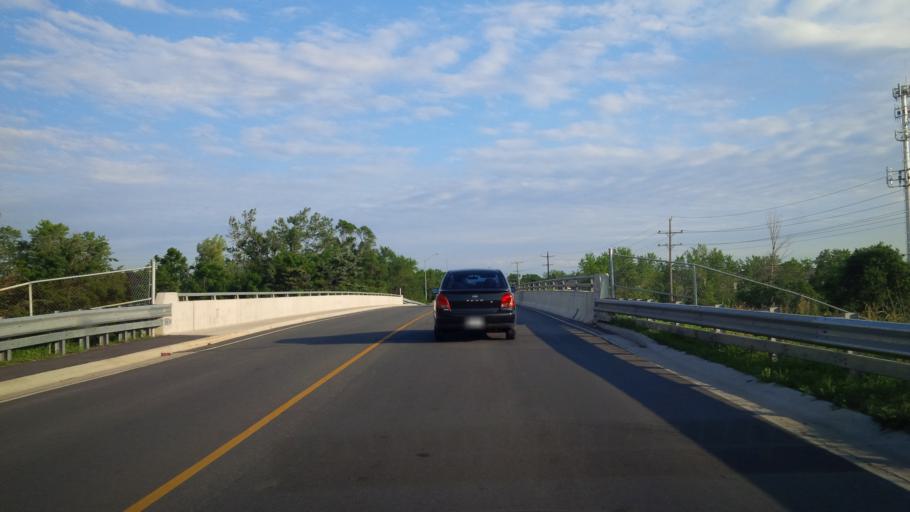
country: CA
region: Ontario
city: Ancaster
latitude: 43.2059
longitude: -79.9836
